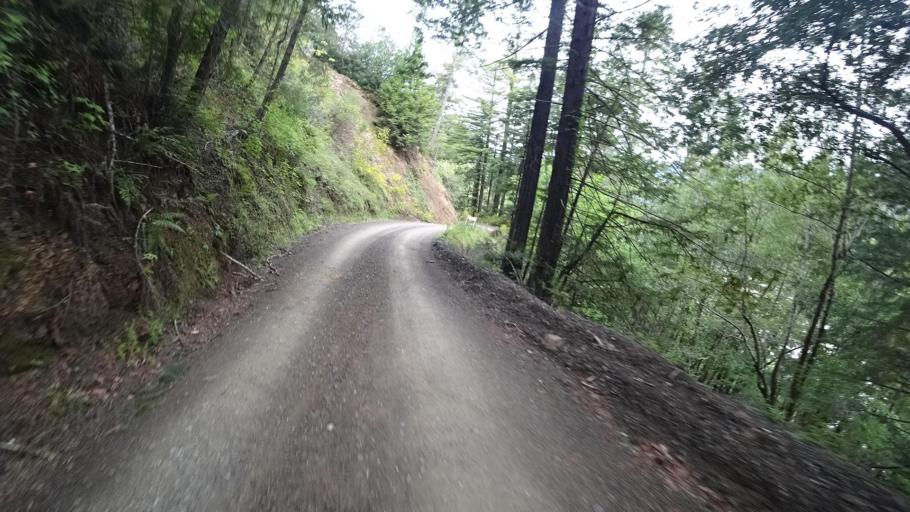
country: US
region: California
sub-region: Humboldt County
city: Redway
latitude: 40.3206
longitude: -123.8330
